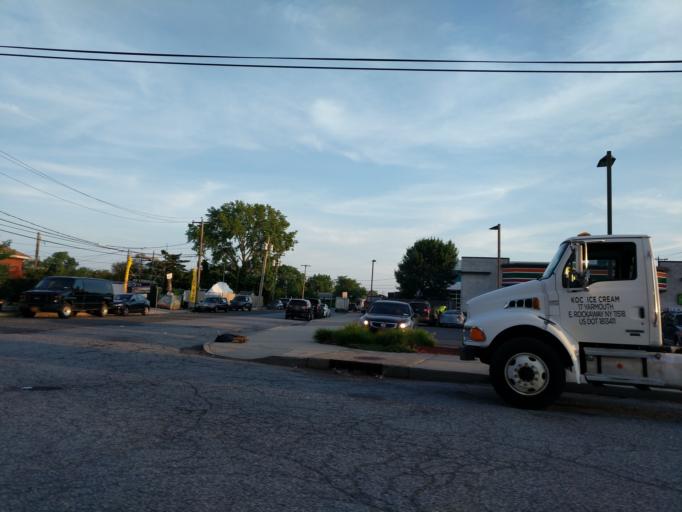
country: US
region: New York
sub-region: Nassau County
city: Barnum Island
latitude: 40.6123
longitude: -73.6438
